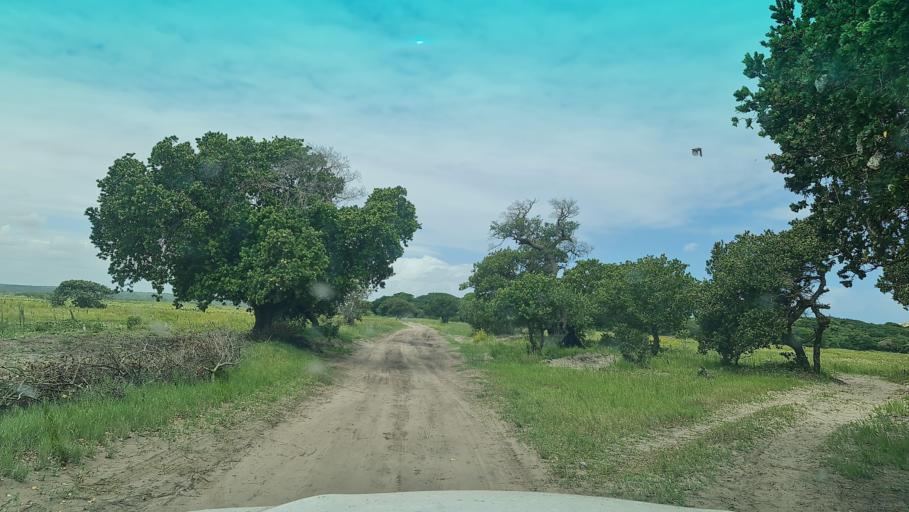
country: MZ
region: Maputo
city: Manhica
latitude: -25.5291
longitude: 32.8488
